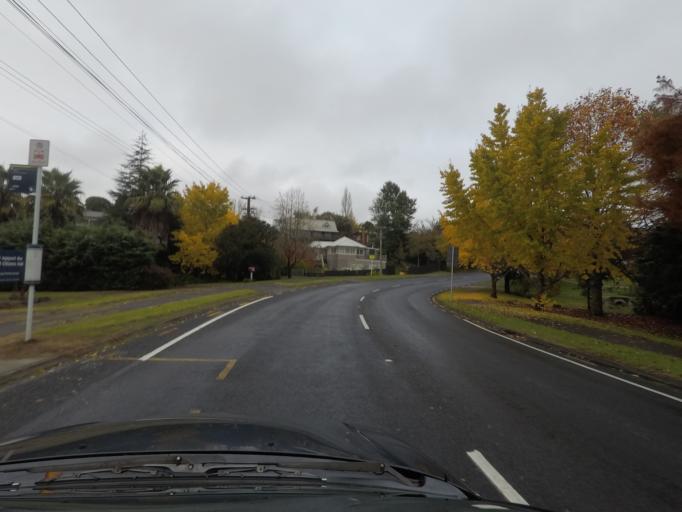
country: NZ
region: Auckland
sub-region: Auckland
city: Rosebank
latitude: -36.7550
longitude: 174.5943
